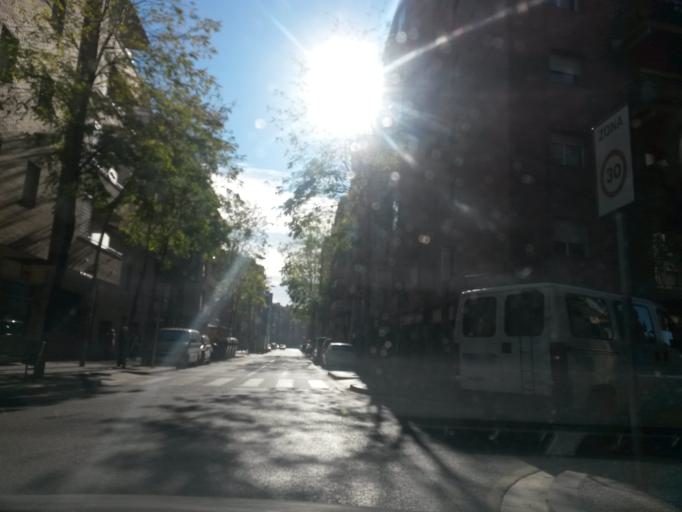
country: ES
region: Catalonia
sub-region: Provincia de Girona
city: Salt
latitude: 41.9758
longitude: 2.8028
